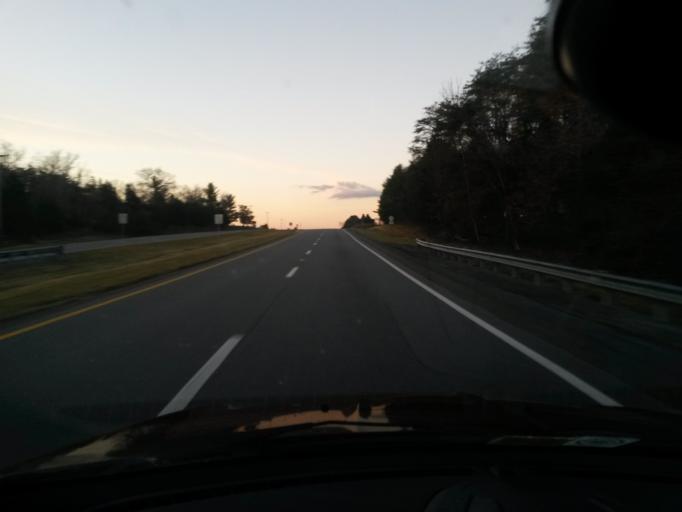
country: US
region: Virginia
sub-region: Botetourt County
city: Fincastle
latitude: 37.5505
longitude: -79.8559
